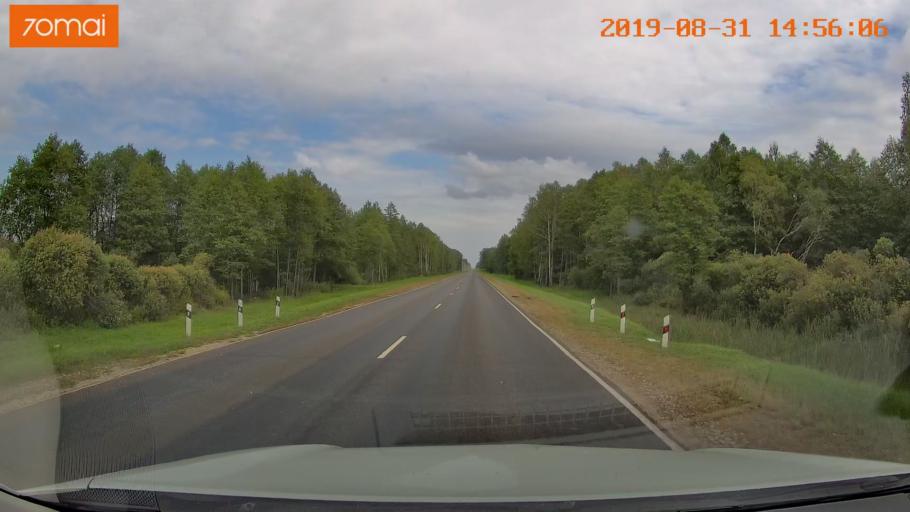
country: RU
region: Kaluga
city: Spas-Demensk
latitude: 54.3027
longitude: 33.9308
